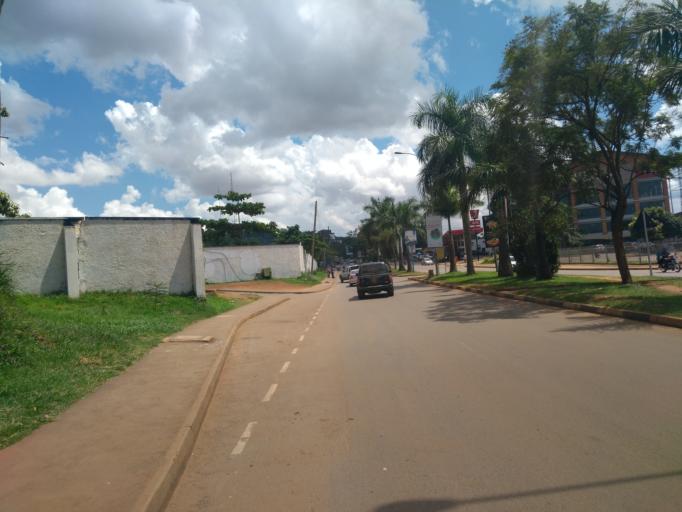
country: UG
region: Central Region
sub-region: Kampala District
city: Kampala
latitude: 0.3260
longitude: 32.6059
